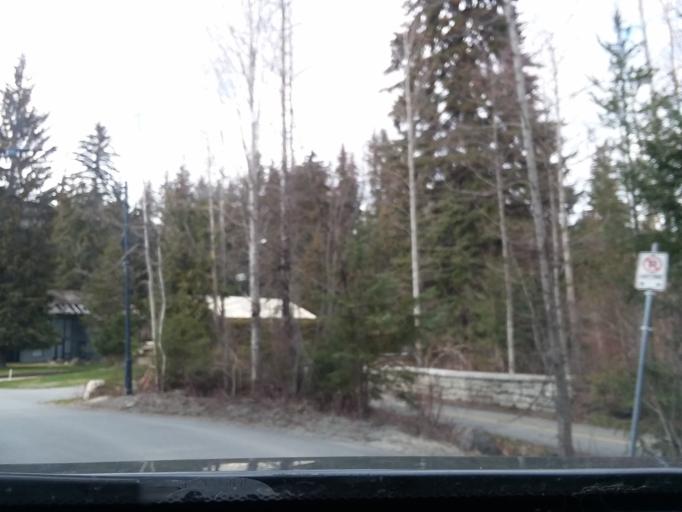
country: CA
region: British Columbia
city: Whistler
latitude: 50.1222
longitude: -122.9697
